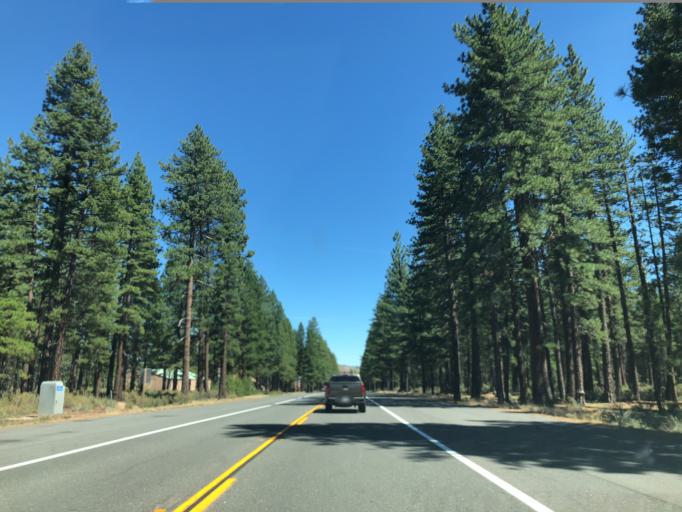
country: US
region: California
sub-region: Lassen County
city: Susanville
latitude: 40.4150
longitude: -120.7621
